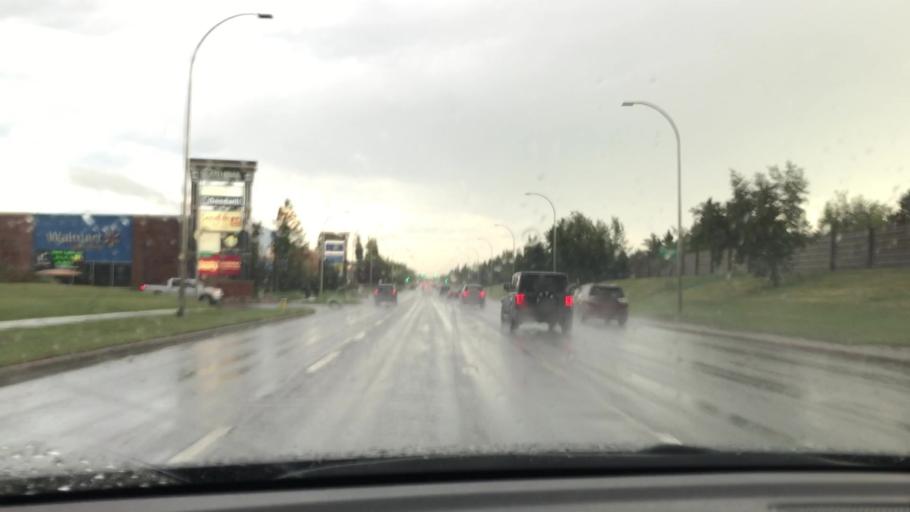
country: CA
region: Alberta
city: Edmonton
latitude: 53.4765
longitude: -113.4956
